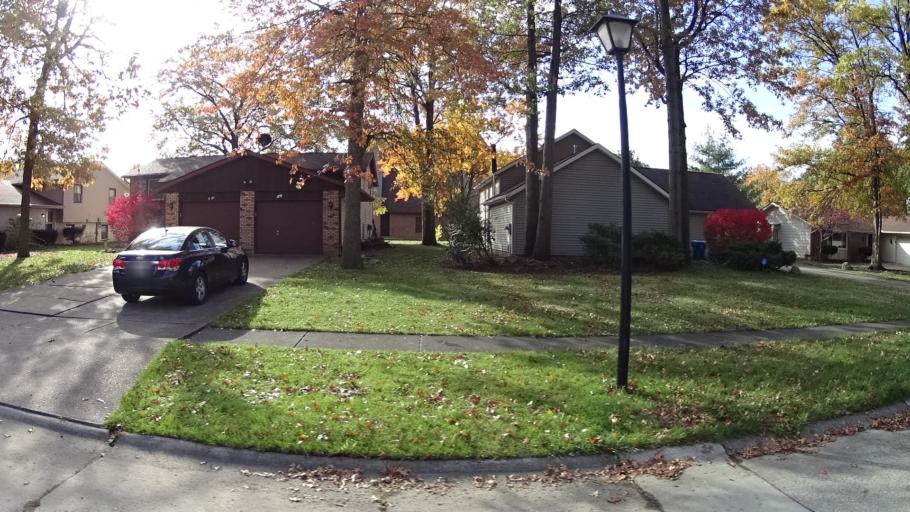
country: US
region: Ohio
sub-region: Lorain County
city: Lorain
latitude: 41.4262
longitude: -82.1906
